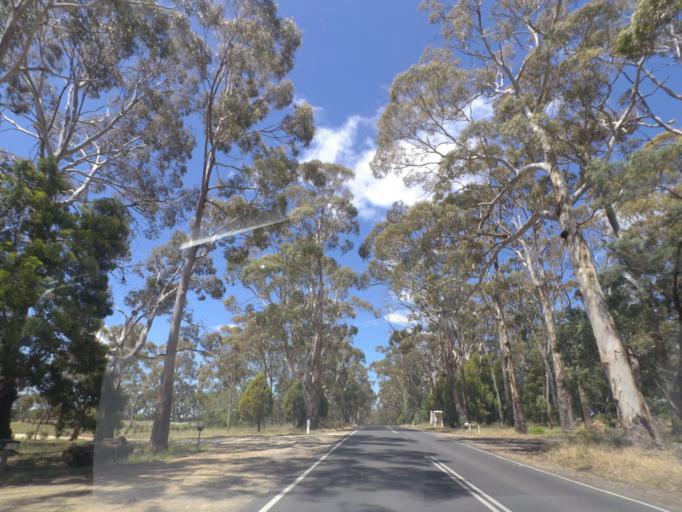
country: AU
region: Victoria
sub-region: Mount Alexander
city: Castlemaine
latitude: -37.2890
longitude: 144.2699
